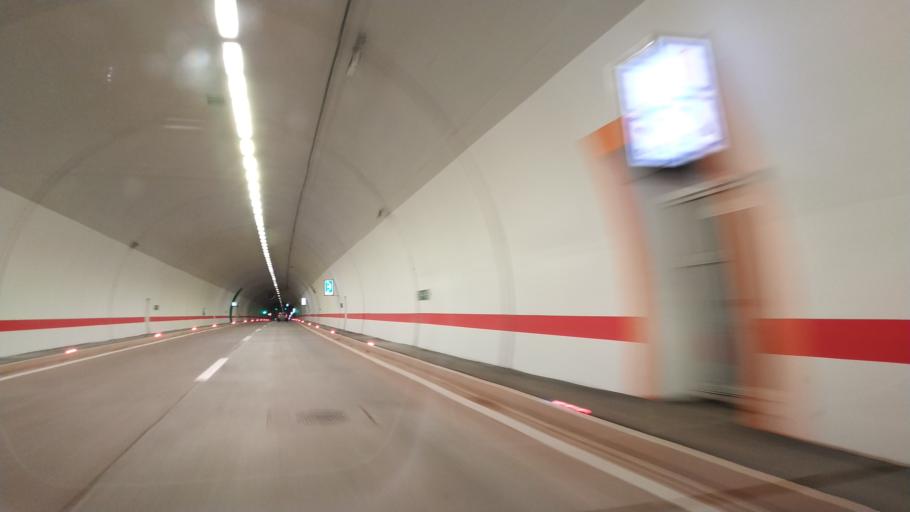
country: RS
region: Central Serbia
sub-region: Nisavski Okrug
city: Gadzin Han
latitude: 43.2689
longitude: 22.1410
